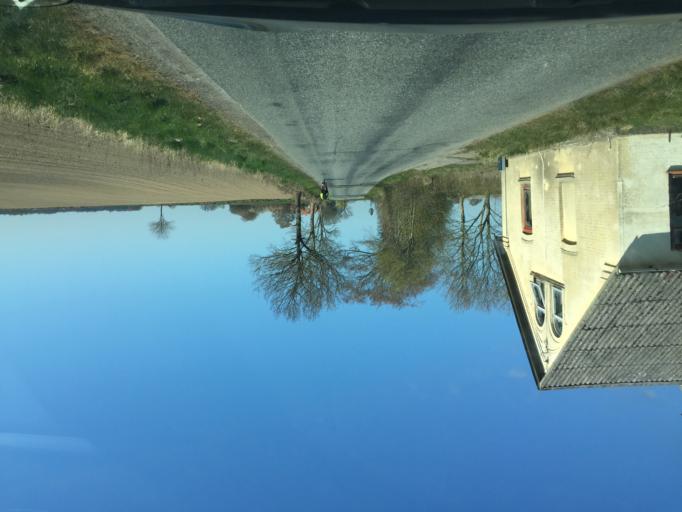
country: DK
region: South Denmark
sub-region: Faaborg-Midtfyn Kommune
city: Ringe
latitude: 55.2547
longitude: 10.5132
